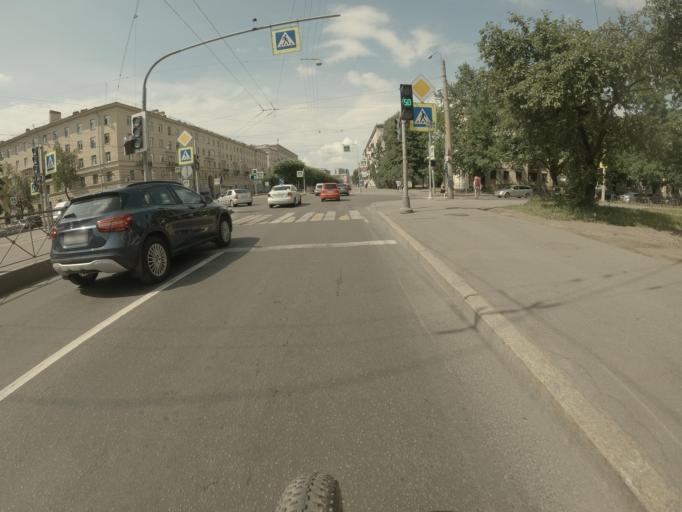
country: RU
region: St.-Petersburg
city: Centralniy
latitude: 59.9247
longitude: 30.4167
